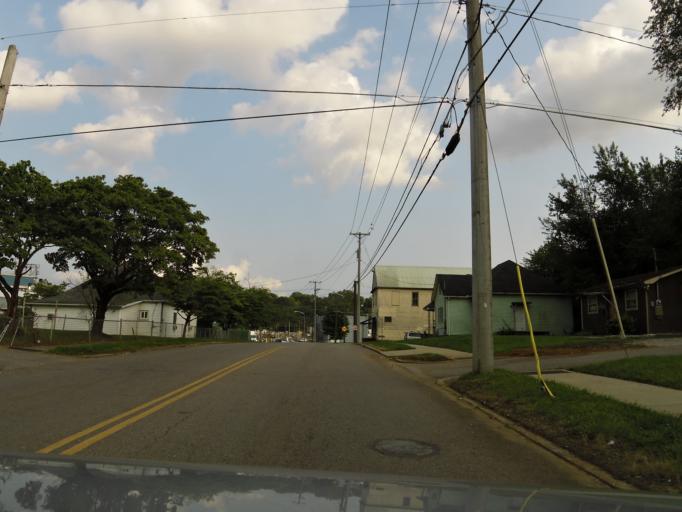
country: US
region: Tennessee
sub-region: Knox County
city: Knoxville
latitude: 35.9855
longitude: -83.9519
